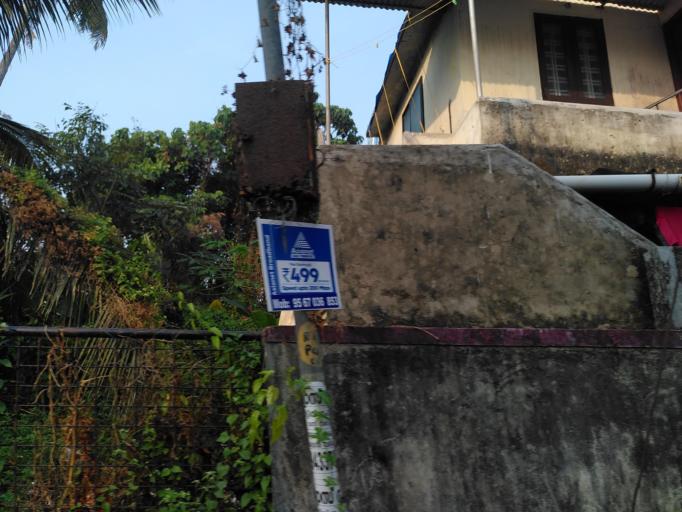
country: IN
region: Kerala
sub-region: Ernakulam
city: Cochin
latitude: 9.9337
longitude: 76.3248
